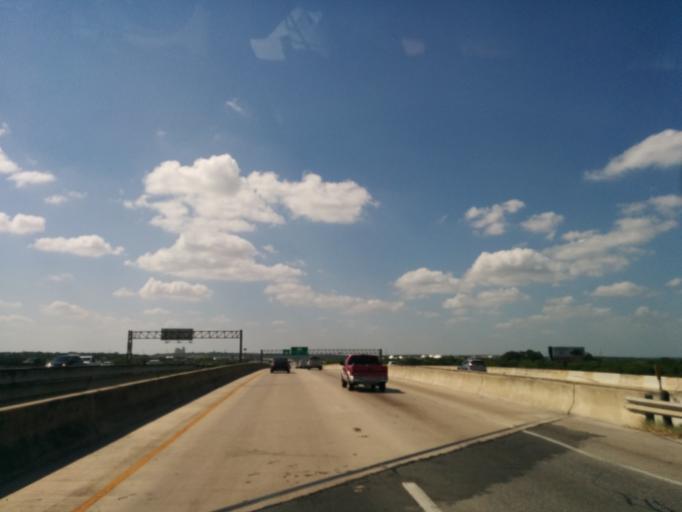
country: US
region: Texas
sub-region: Bexar County
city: Live Oak
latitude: 29.5811
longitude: -98.3444
